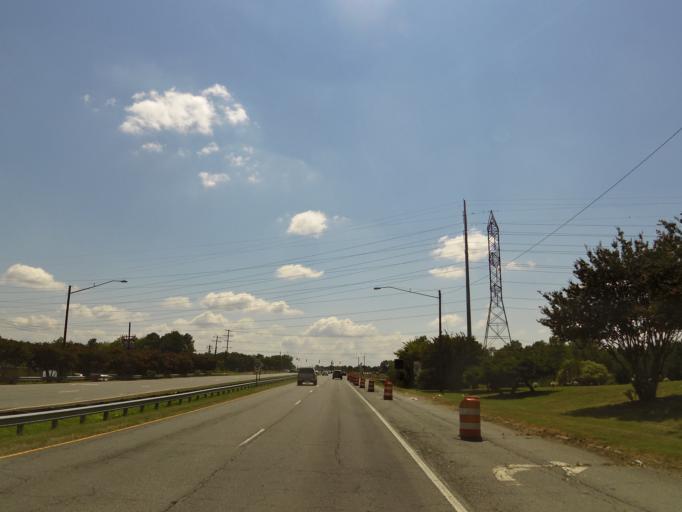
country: US
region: North Carolina
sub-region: Cabarrus County
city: Kannapolis
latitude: 35.4499
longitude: -80.6099
